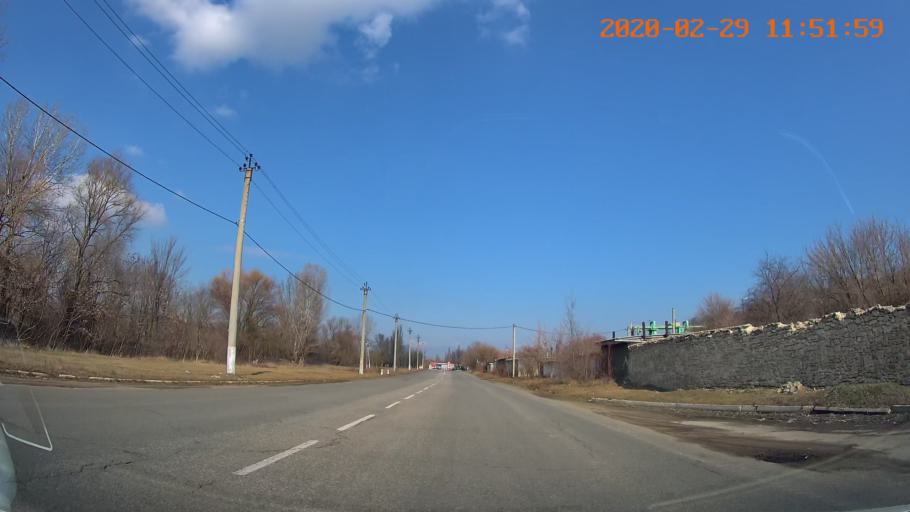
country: MD
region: Telenesti
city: Ribnita
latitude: 47.7684
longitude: 28.9912
